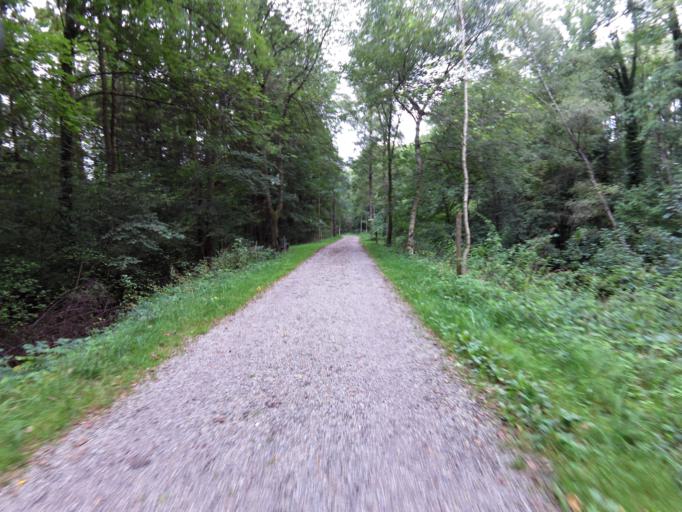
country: DE
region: Bavaria
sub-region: Lower Bavaria
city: Landshut
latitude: 48.5276
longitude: 12.1290
